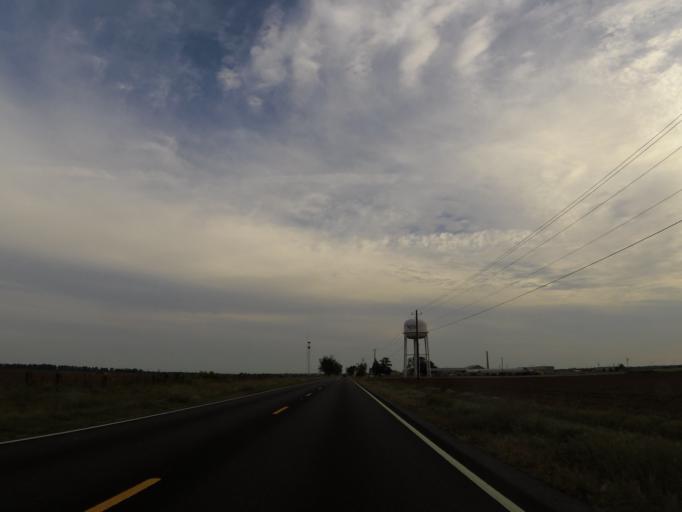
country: US
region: Alabama
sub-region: Escambia County
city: Atmore
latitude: 31.1631
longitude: -87.4636
